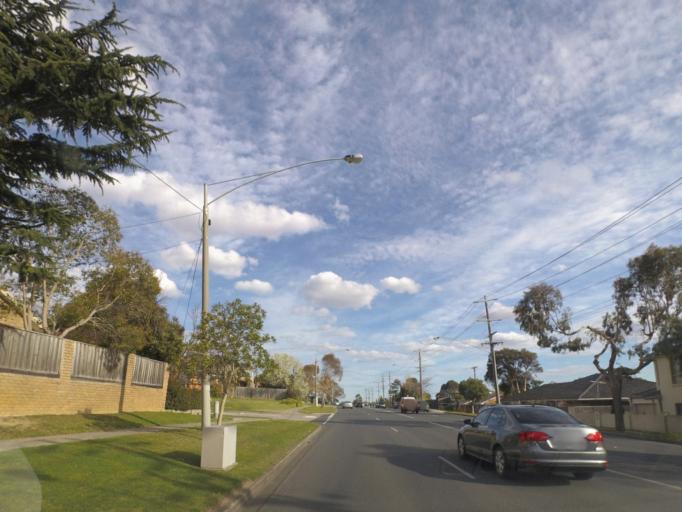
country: AU
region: Victoria
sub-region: Manningham
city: Doncaster East
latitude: -37.7926
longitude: 145.1428
